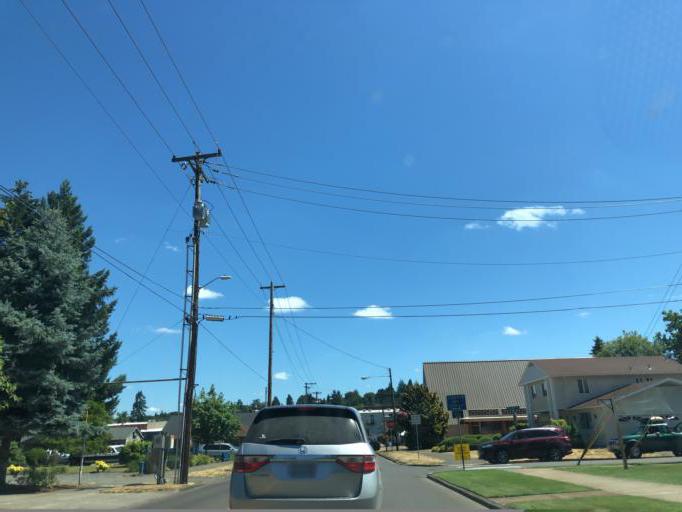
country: US
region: Oregon
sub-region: Marion County
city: Silverton
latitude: 45.0040
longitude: -122.7854
